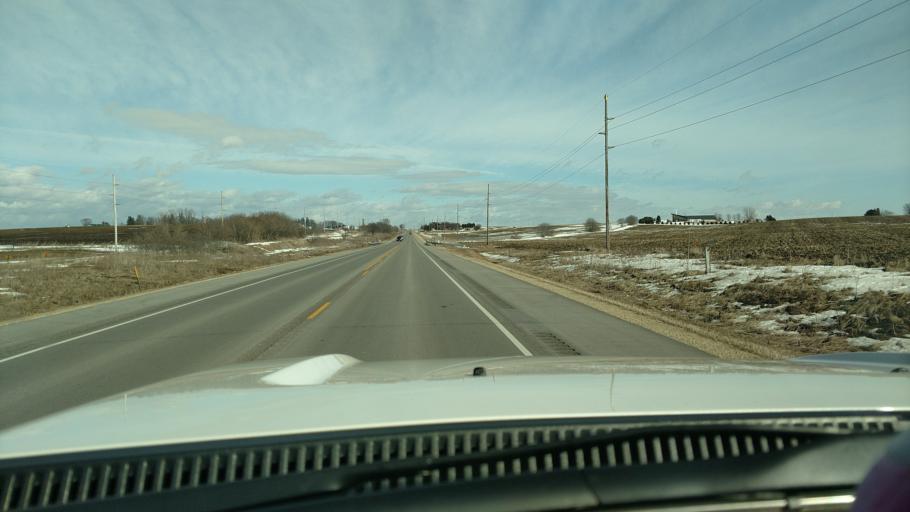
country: US
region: Minnesota
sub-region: Wabasha County
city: Elgin
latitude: 44.1427
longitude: -92.2315
